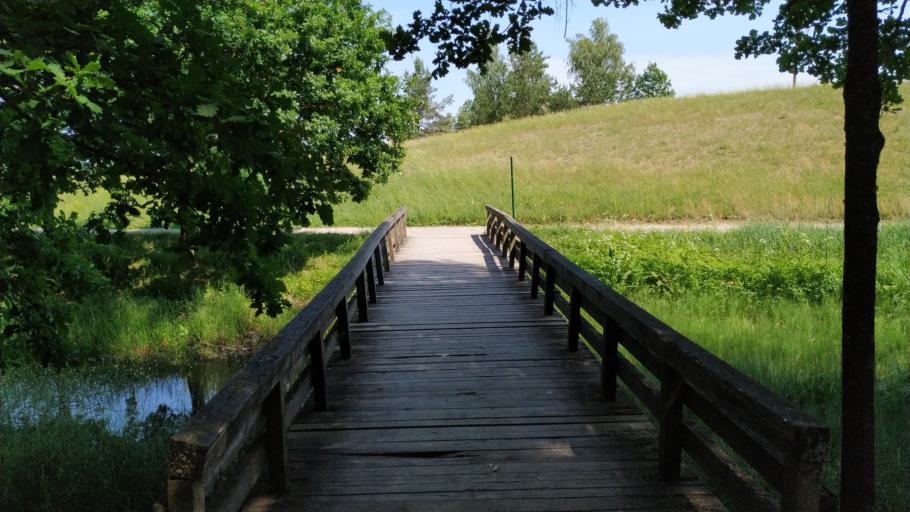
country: LT
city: Nemencine
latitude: 54.9071
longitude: 25.3200
